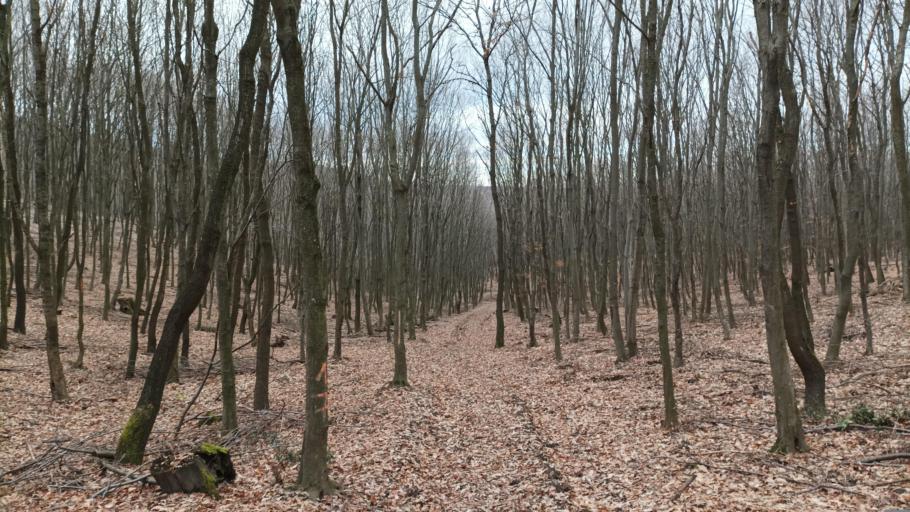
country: HU
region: Tolna
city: Szentgalpuszta
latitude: 46.3213
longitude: 18.6376
